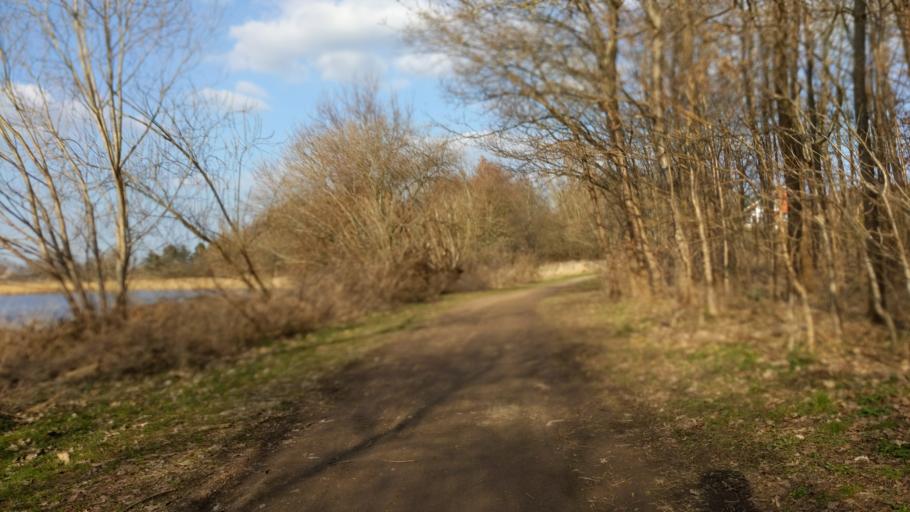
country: DE
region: Schleswig-Holstein
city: Neustadt in Holstein
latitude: 54.1132
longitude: 10.8187
